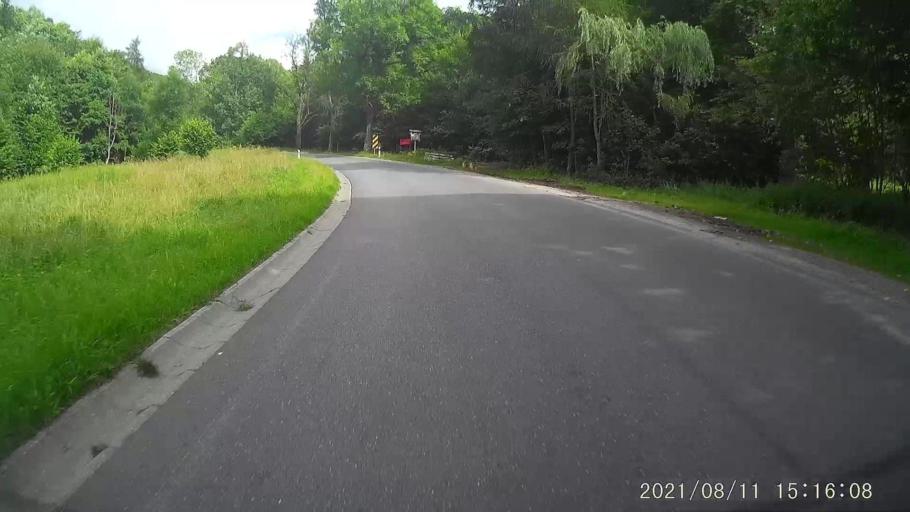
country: PL
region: Lower Silesian Voivodeship
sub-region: Powiat klodzki
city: Stronie Slaskie
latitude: 50.2668
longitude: 16.7605
